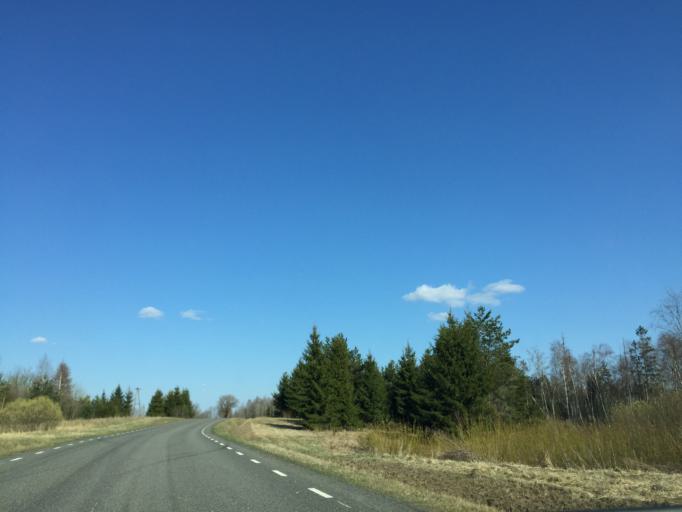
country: EE
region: Viljandimaa
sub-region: Viiratsi vald
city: Viiratsi
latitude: 58.2699
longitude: 25.6751
